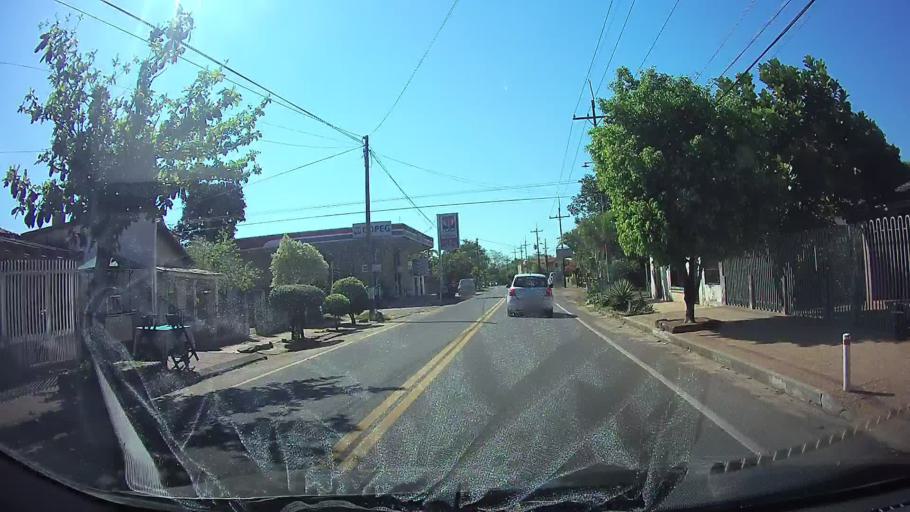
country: PY
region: Central
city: Ypacarai
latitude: -25.3980
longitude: -57.2926
